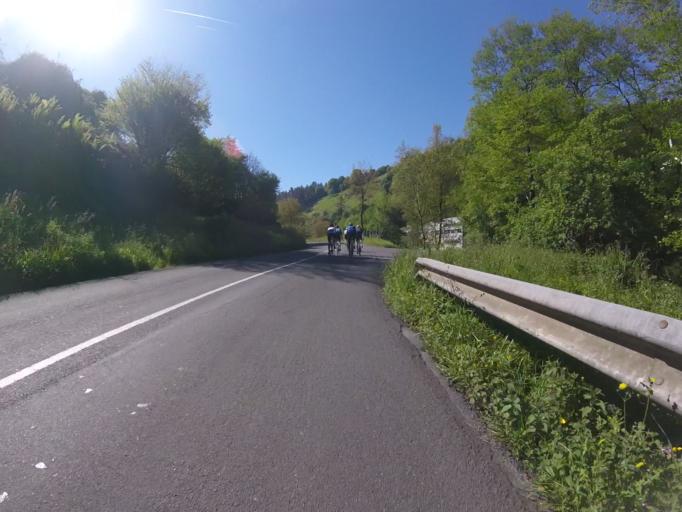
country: ES
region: Basque Country
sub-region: Provincia de Guipuzcoa
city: Errezil
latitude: 43.1715
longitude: -2.1986
